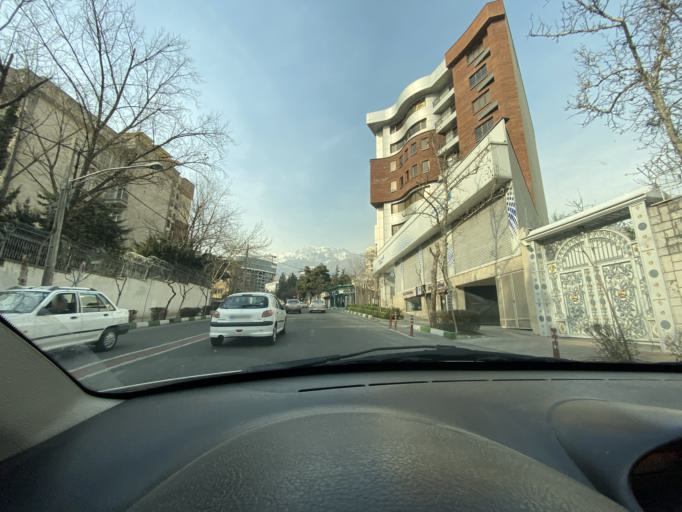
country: IR
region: Tehran
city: Tajrish
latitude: 35.8027
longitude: 51.4786
